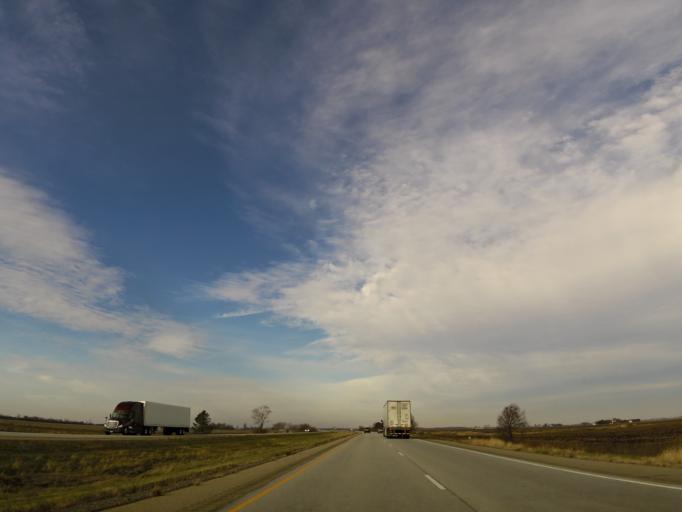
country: US
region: Illinois
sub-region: De Witt County
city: Farmer City
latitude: 40.2283
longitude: -88.5438
